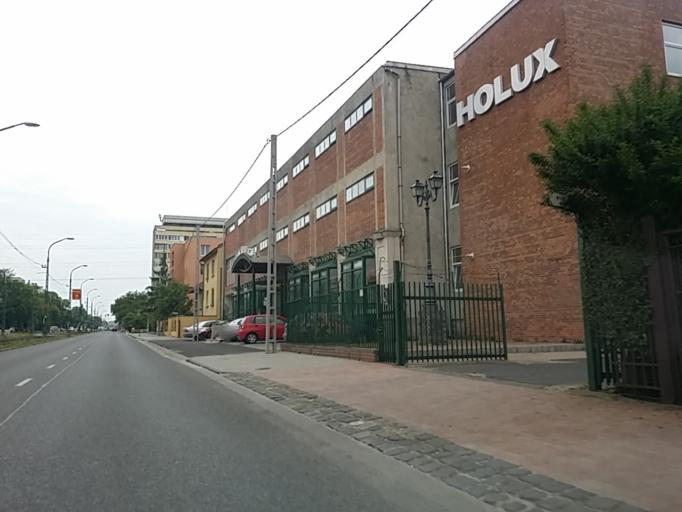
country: HU
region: Budapest
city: Budapest XIII. keruelet
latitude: 47.5373
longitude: 19.0842
